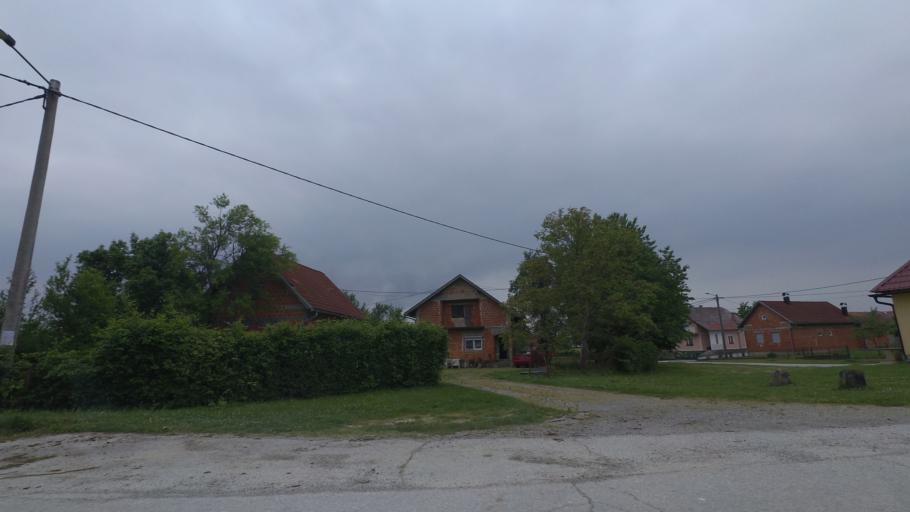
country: HR
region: Sisacko-Moslavacka
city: Gvozd
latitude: 45.2929
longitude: 15.9541
